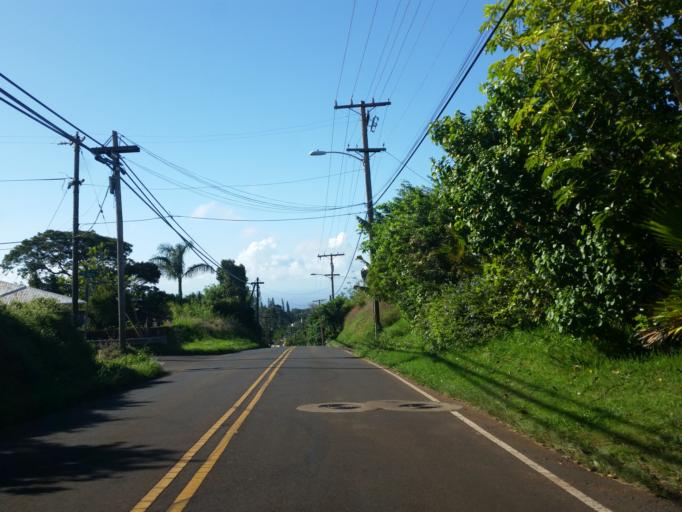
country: US
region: Hawaii
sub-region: Maui County
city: Makawao
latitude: 20.8508
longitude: -156.3089
